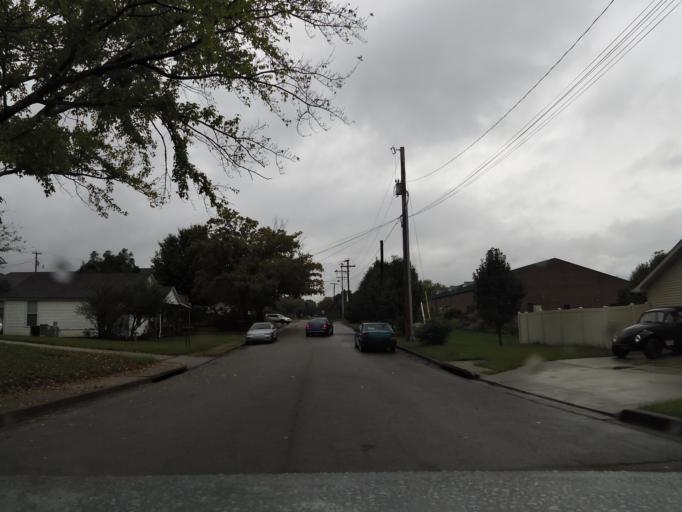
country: US
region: Tennessee
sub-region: Blount County
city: Maryville
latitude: 35.7731
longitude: -83.9575
